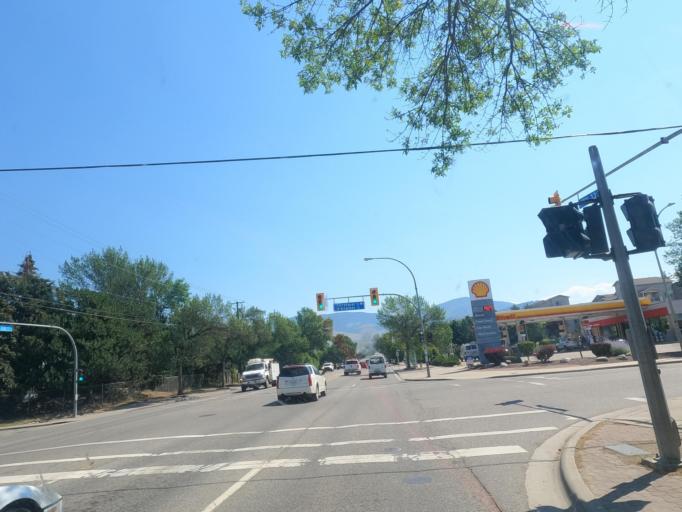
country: CA
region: British Columbia
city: Kelowna
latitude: 49.8890
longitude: -119.4096
